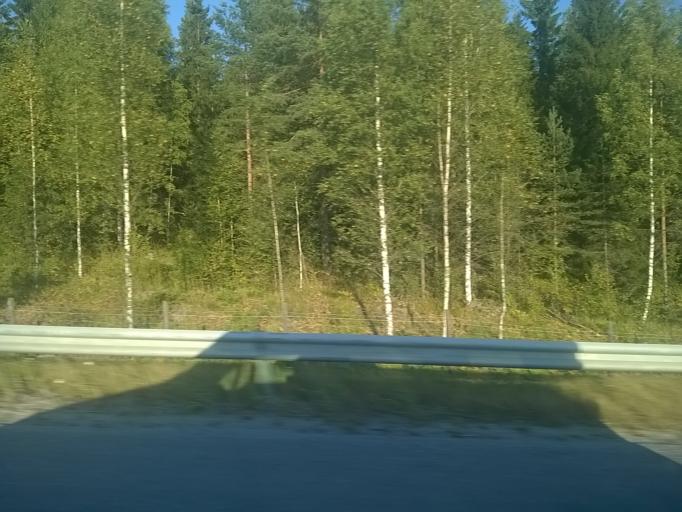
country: FI
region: Pirkanmaa
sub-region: Tampere
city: Tampere
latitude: 61.4306
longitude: 23.7549
